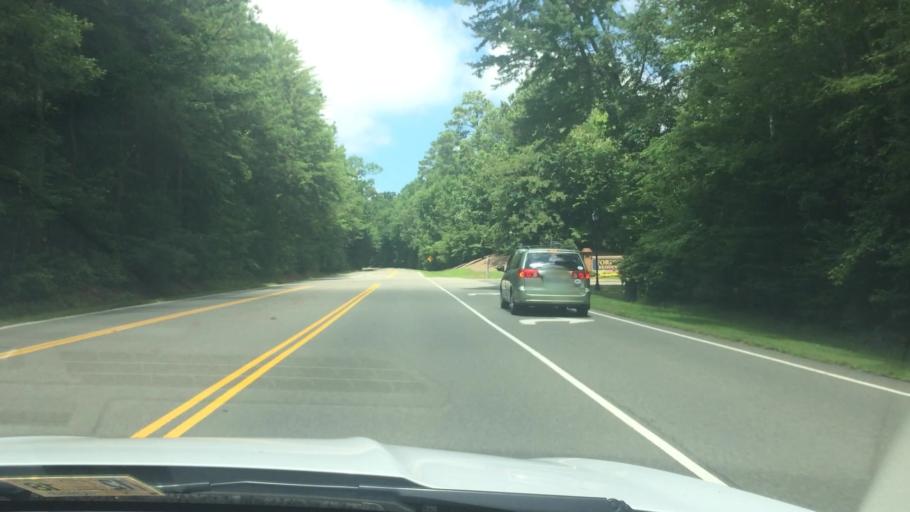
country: US
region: Virginia
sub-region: James City County
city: Williamsburg
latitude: 37.2780
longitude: -76.7779
